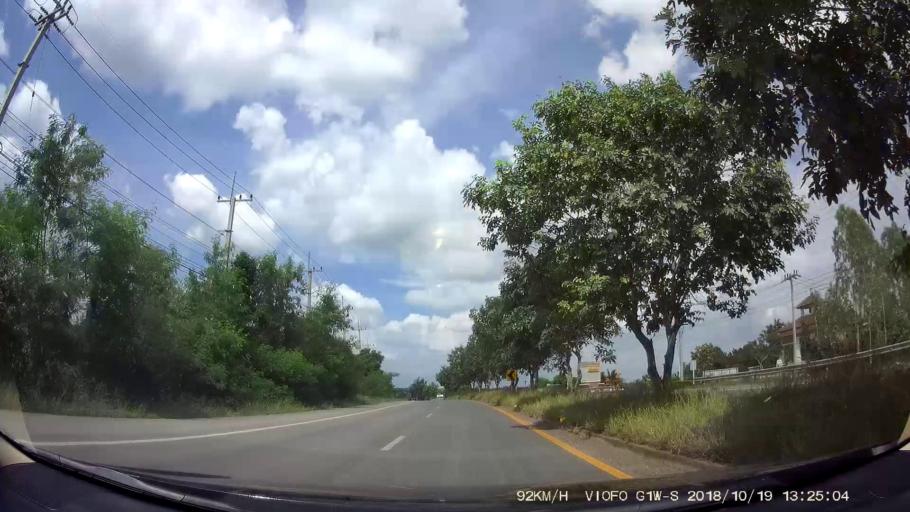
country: TH
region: Chaiyaphum
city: Chatturat
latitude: 15.5160
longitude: 101.8247
